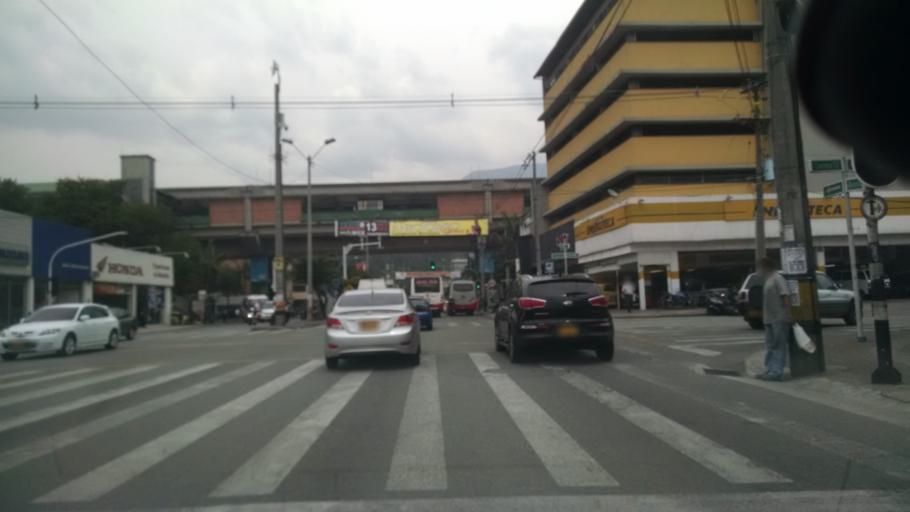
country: CO
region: Antioquia
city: Medellin
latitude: 6.2387
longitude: -75.5740
